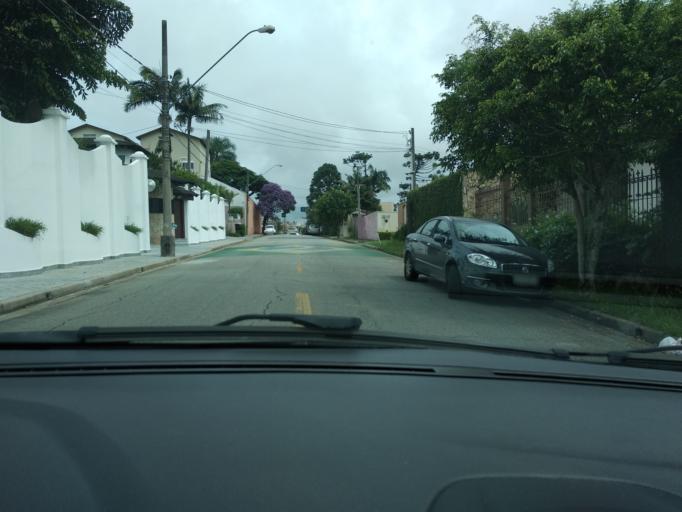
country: BR
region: Sao Paulo
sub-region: Mogi das Cruzes
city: Mogi das Cruzes
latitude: -23.5278
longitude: -46.1773
